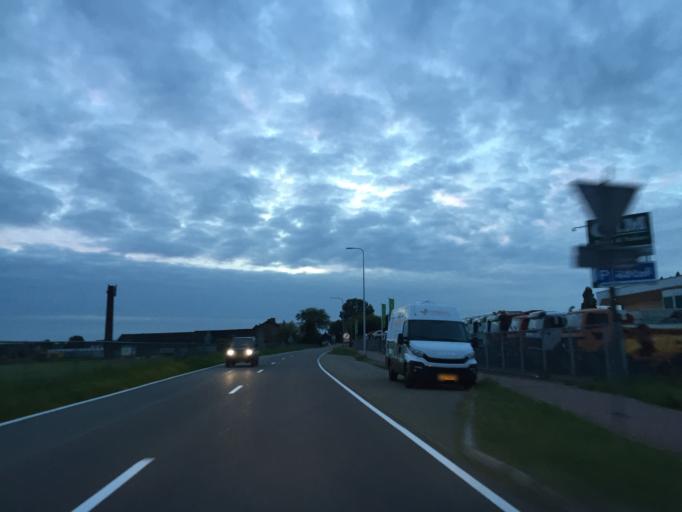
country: NL
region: South Holland
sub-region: Gemeente Zoetermeer
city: Zoetermeer
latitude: 52.0344
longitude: 4.4750
